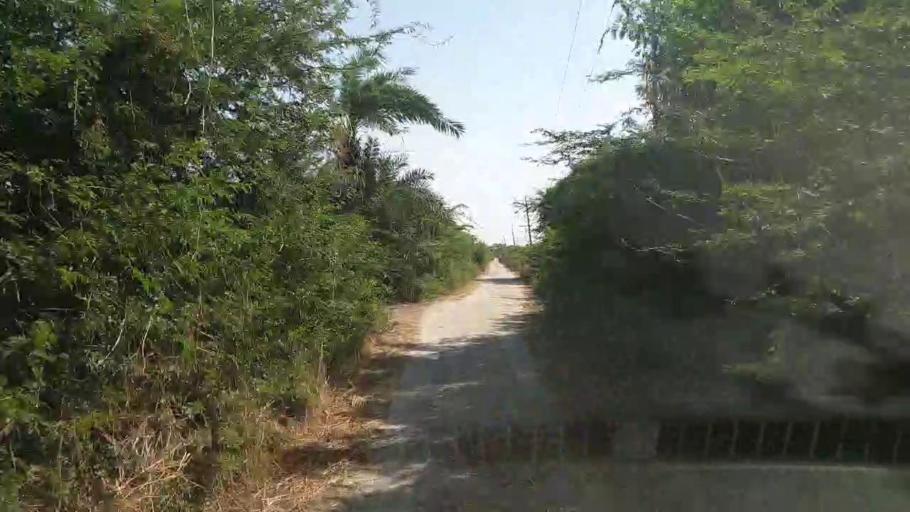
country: PK
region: Sindh
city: Tando Bago
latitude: 24.6458
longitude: 68.9865
